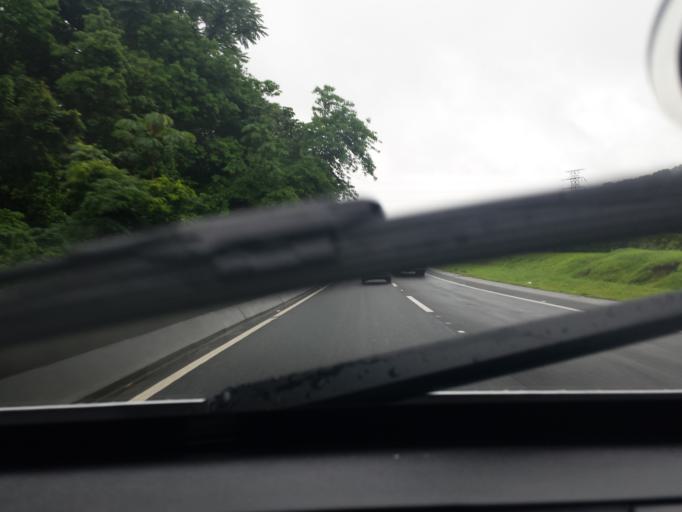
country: BR
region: Santa Catarina
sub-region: Itapema
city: Itapema
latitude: -27.0364
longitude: -48.6039
